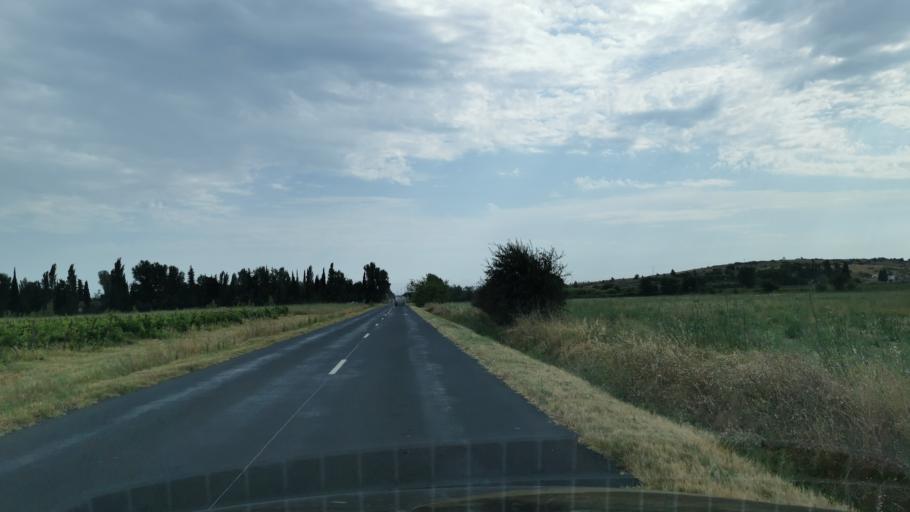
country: FR
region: Languedoc-Roussillon
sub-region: Departement de l'Aude
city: Ouveillan
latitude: 43.2721
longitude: 3.0144
